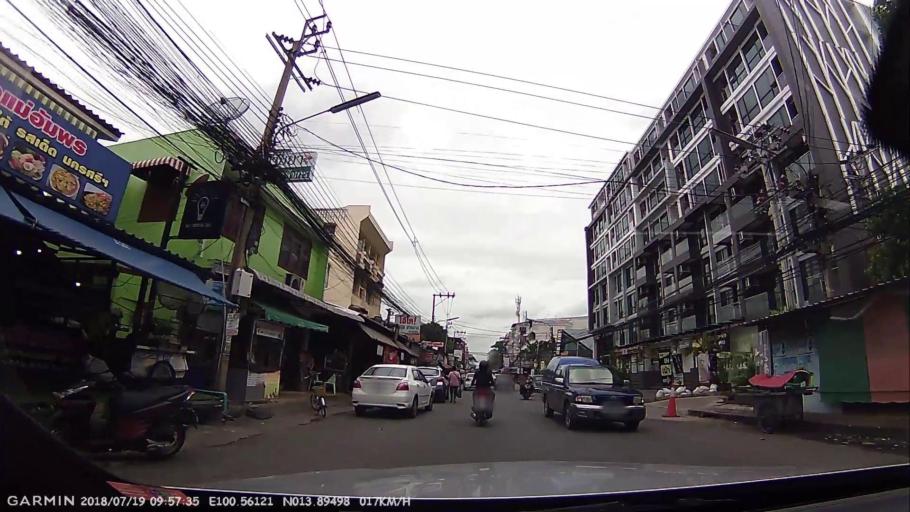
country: TH
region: Bangkok
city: Lak Si
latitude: 13.8950
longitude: 100.5612
